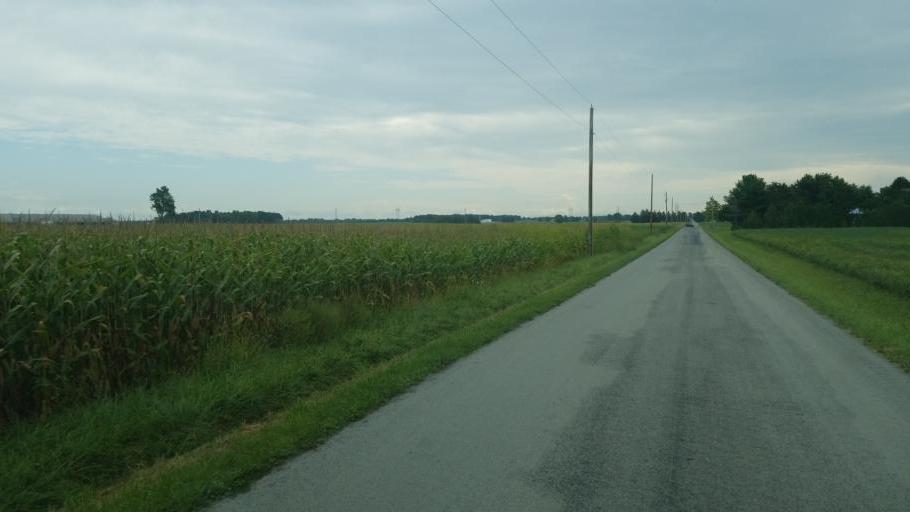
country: US
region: Ohio
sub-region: Wyandot County
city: Upper Sandusky
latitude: 40.9062
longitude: -83.1739
